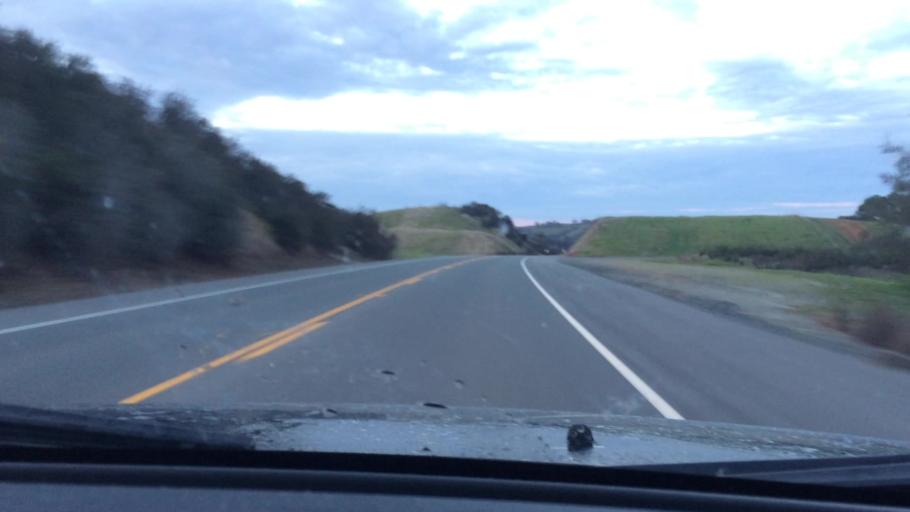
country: US
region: California
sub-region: Amador County
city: Ione
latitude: 38.3975
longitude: -120.8957
